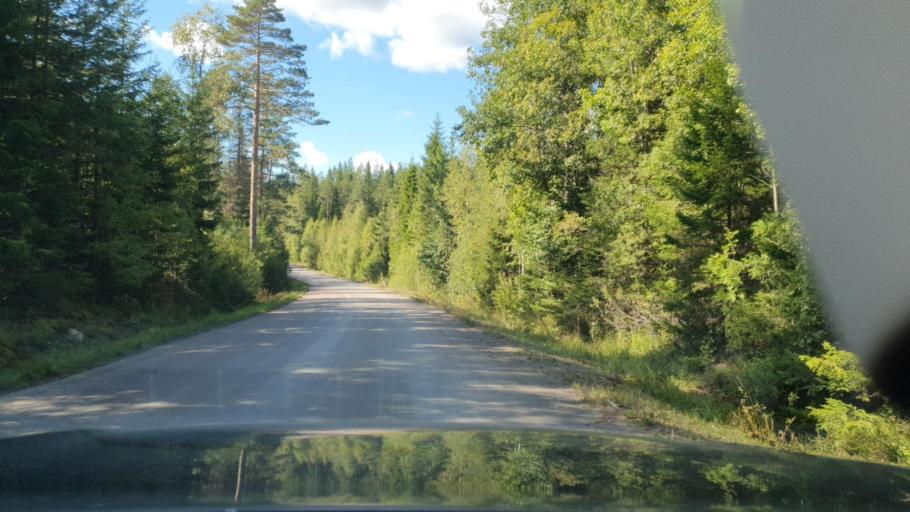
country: SE
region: Vaermland
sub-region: Filipstads Kommun
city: Filipstad
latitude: 59.7274
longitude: 14.2188
